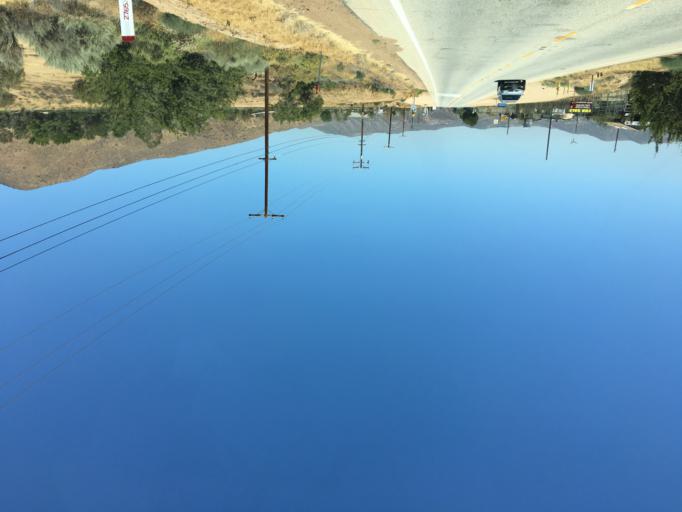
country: US
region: California
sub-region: Los Angeles County
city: Acton
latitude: 34.4937
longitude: -118.1921
